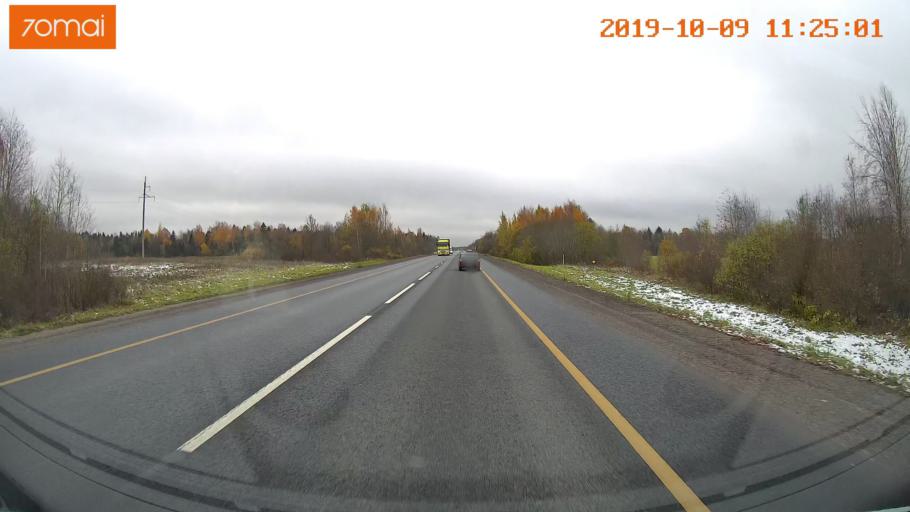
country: RU
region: Vologda
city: Vologda
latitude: 59.1058
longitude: 39.9863
